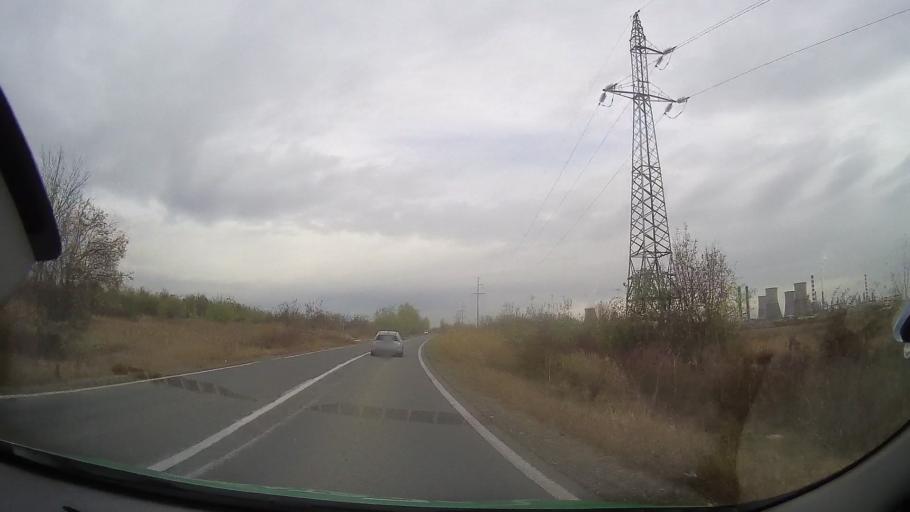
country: RO
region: Prahova
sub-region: Comuna Bucov
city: Bucov
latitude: 44.9545
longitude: 26.0646
